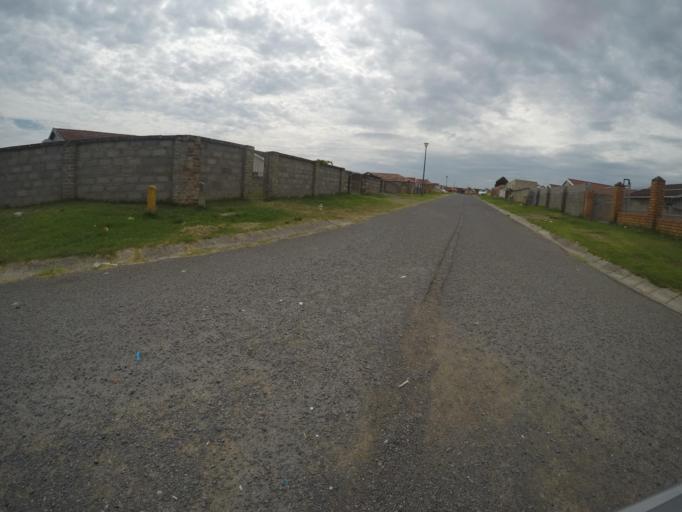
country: ZA
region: Eastern Cape
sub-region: Buffalo City Metropolitan Municipality
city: East London
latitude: -33.0028
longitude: 27.8749
